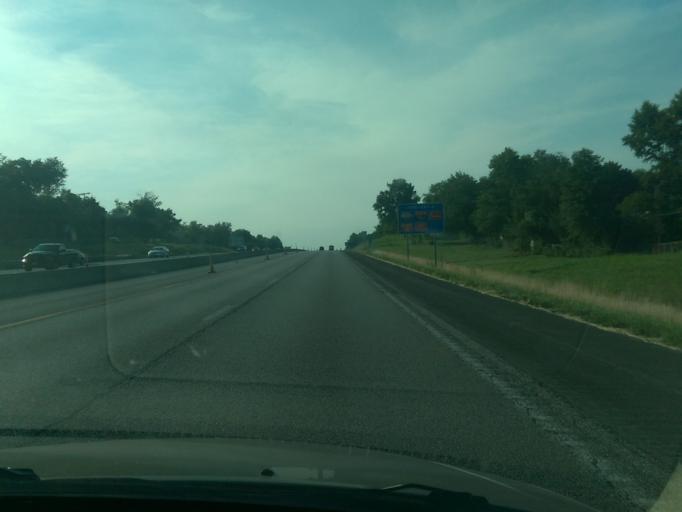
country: US
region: Missouri
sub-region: Platte County
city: Parkville
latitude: 39.2162
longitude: -94.6435
